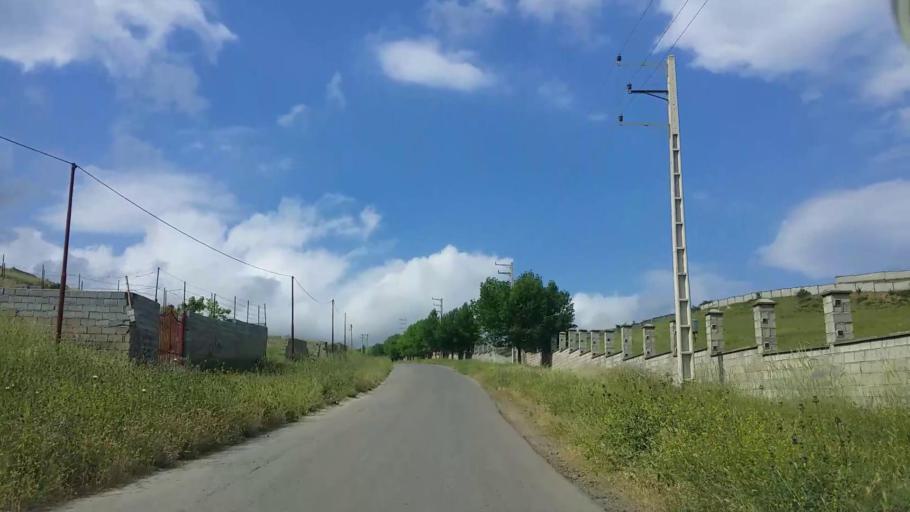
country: IR
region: Mazandaran
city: Chalus
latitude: 36.5285
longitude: 51.2684
